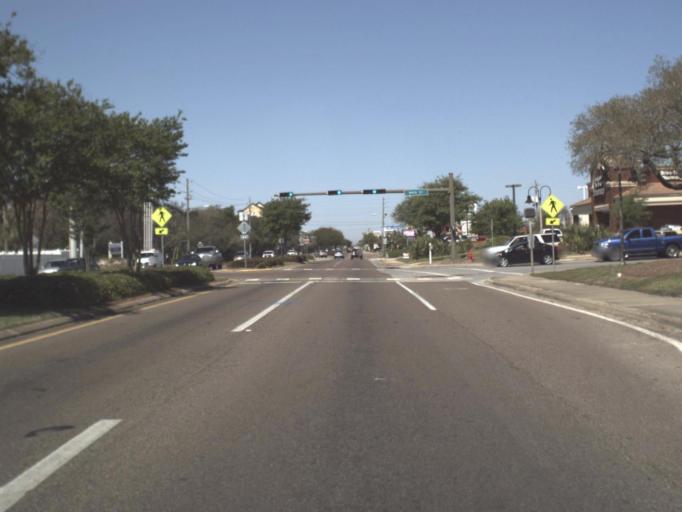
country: US
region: Florida
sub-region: Okaloosa County
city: Destin
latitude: 30.3895
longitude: -86.4830
